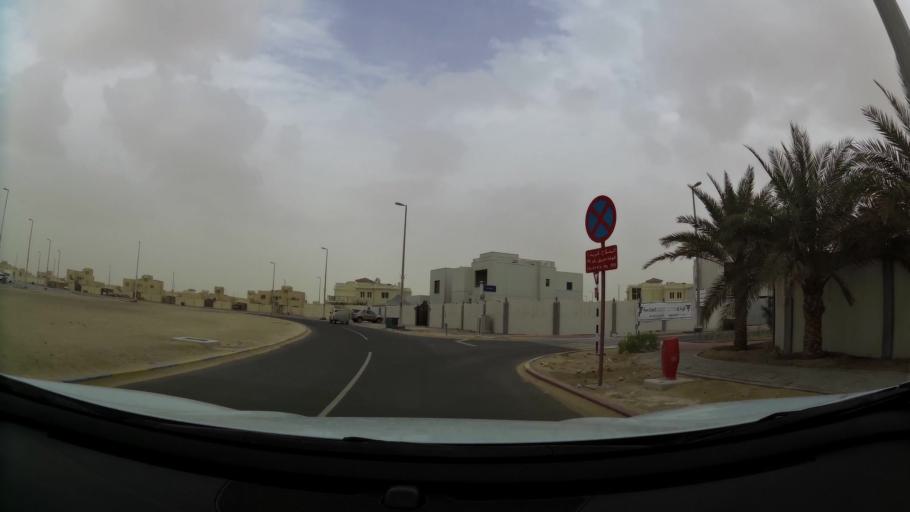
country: AE
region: Abu Dhabi
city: Abu Dhabi
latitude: 24.4469
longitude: 54.7174
